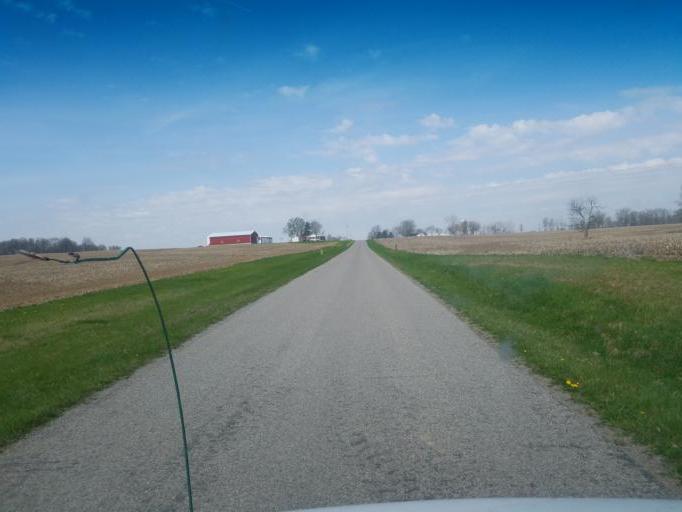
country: US
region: Ohio
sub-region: Logan County
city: Northwood
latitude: 40.5000
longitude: -83.6414
